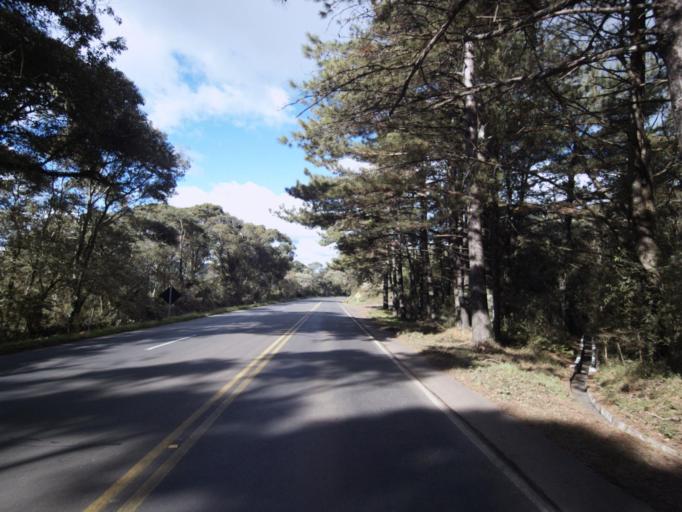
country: BR
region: Santa Catarina
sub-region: Joacaba
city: Joacaba
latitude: -26.9740
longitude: -51.7629
